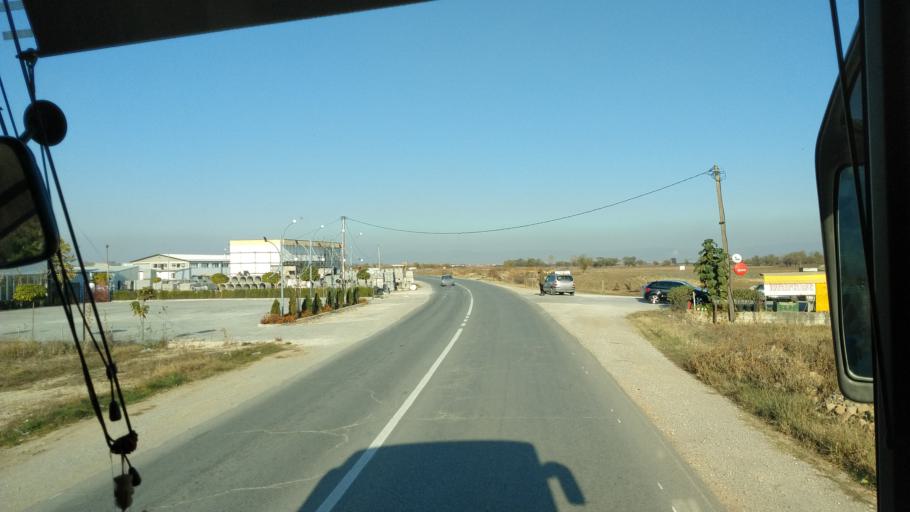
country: XK
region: Ferizaj
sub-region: Komuna e Shtimes
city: Shtime
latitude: 42.4514
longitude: 21.0697
